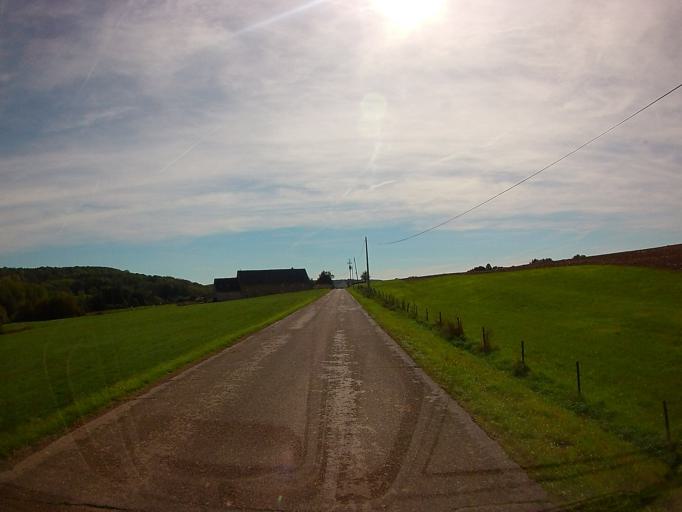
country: BE
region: Wallonia
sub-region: Province de Liege
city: Aubel
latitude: 50.7383
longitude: 5.8928
